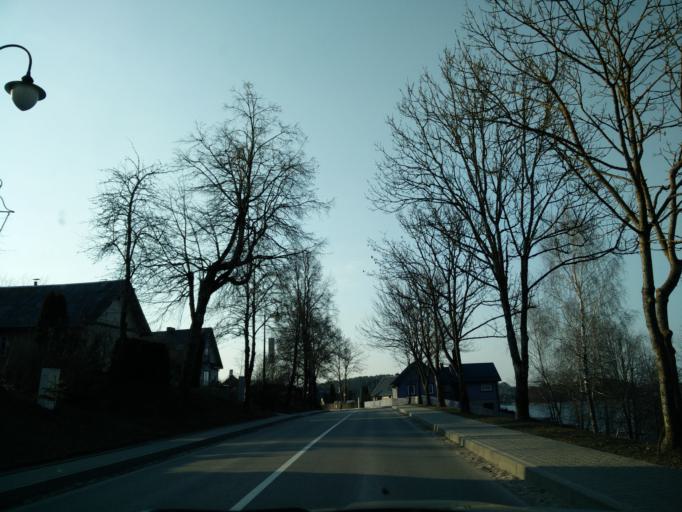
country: LT
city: Trakai
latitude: 54.6517
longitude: 24.9222
